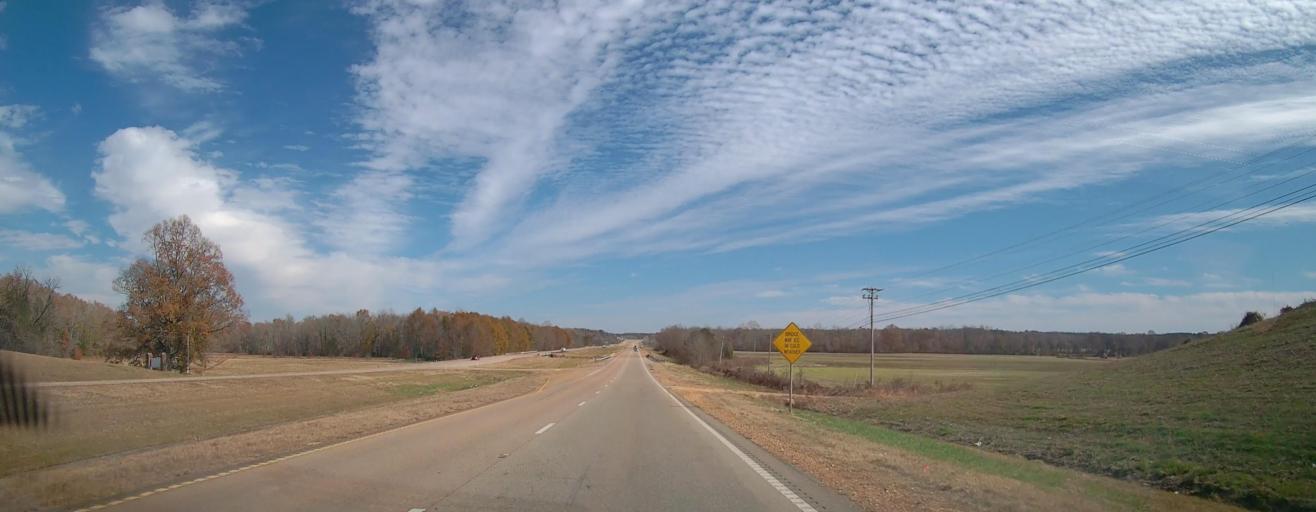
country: US
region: Mississippi
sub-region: Tippah County
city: Ripley
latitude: 34.9521
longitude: -88.8847
